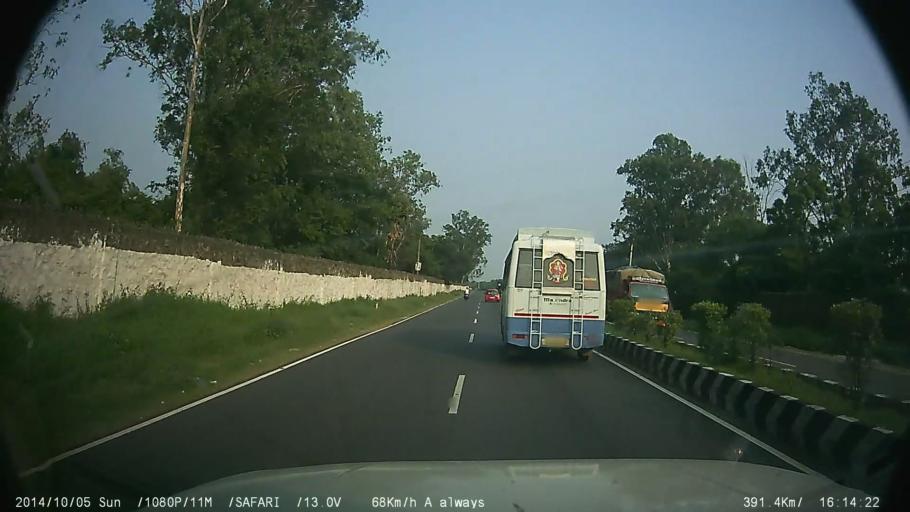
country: IN
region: Tamil Nadu
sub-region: Kancheepuram
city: Vandalur
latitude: 12.8731
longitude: 80.0940
